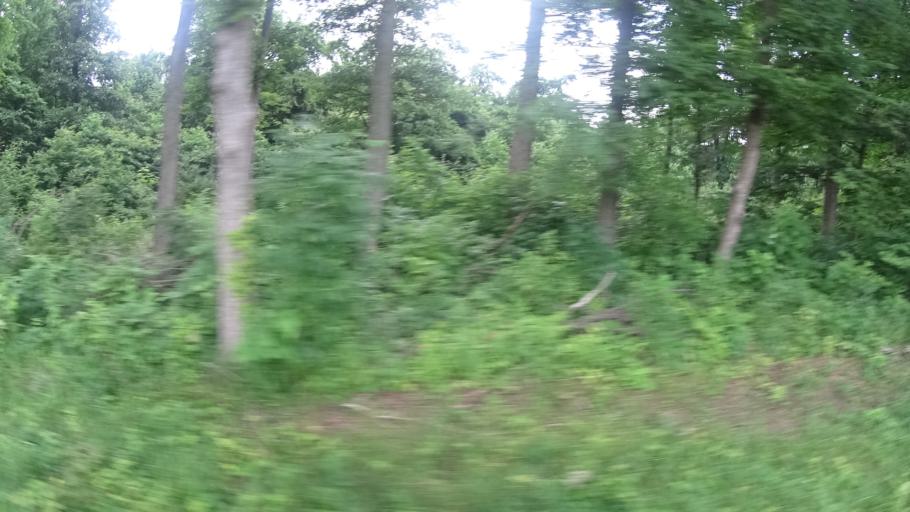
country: US
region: Ohio
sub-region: Erie County
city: Milan
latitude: 41.2969
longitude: -82.5076
